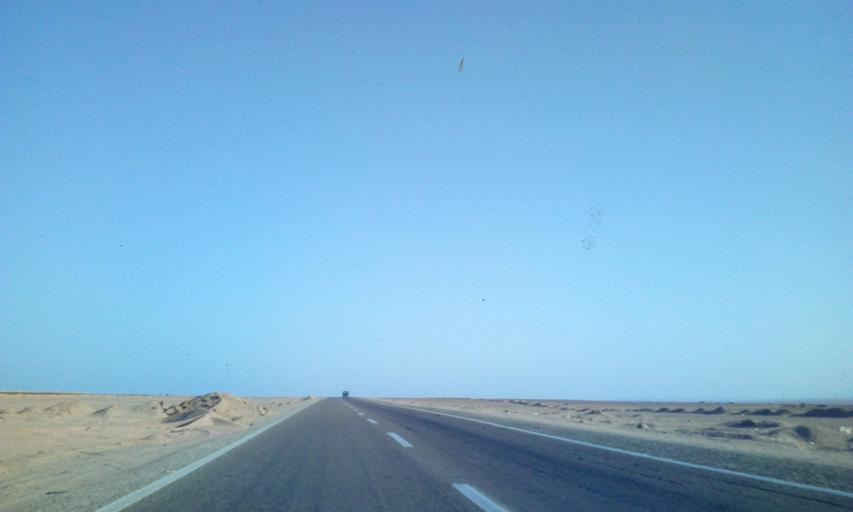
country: EG
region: South Sinai
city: Tor
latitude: 28.4905
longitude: 32.9658
